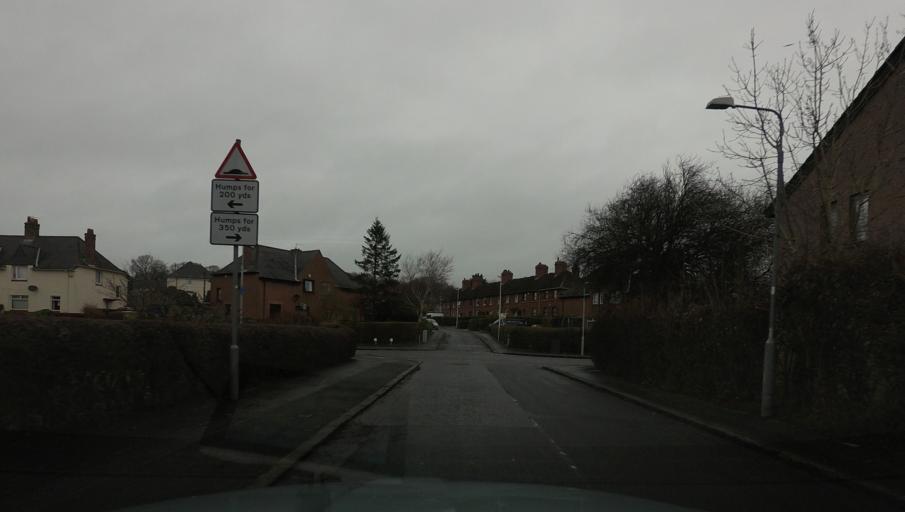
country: GB
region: Scotland
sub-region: Fife
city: Rosyth
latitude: 56.0403
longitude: -3.4192
